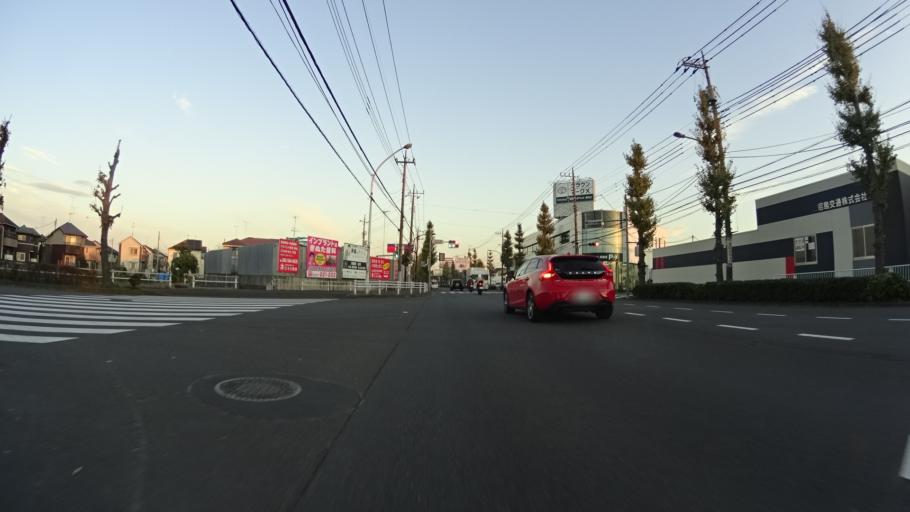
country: JP
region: Tokyo
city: Hino
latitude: 35.6991
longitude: 139.3685
